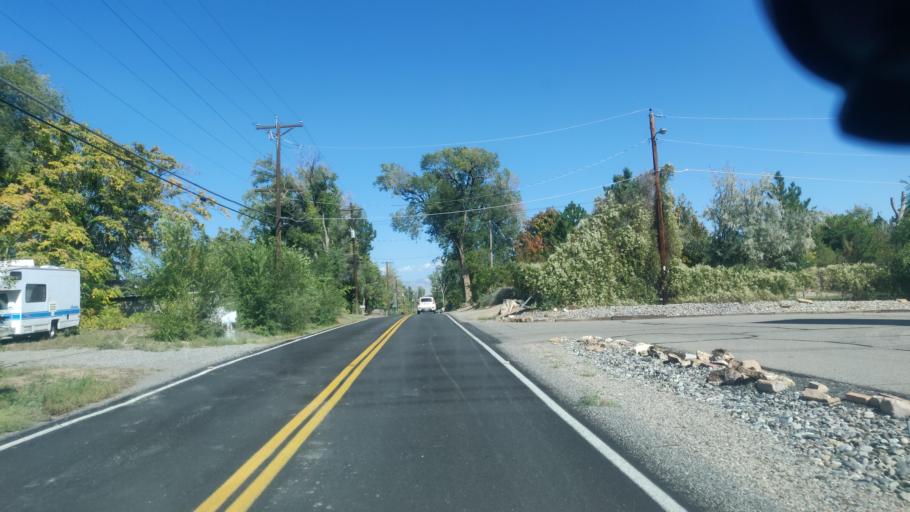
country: US
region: Colorado
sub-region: Mesa County
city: Redlands
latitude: 39.0757
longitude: -108.6264
